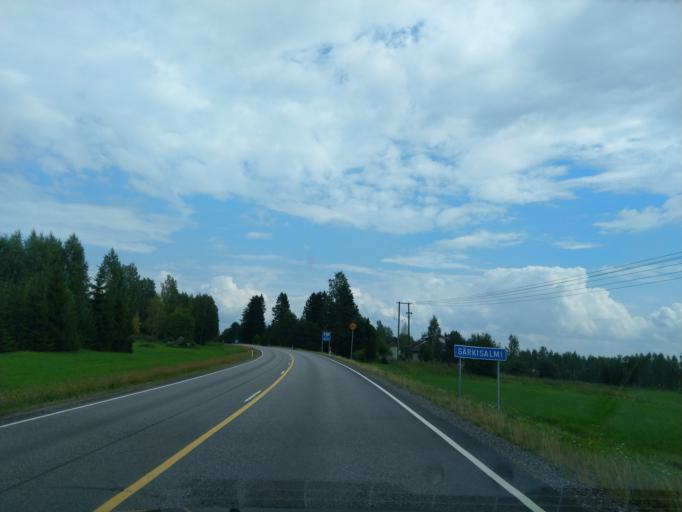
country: FI
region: South Karelia
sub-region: Imatra
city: Parikkala
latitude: 61.6040
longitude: 29.4682
